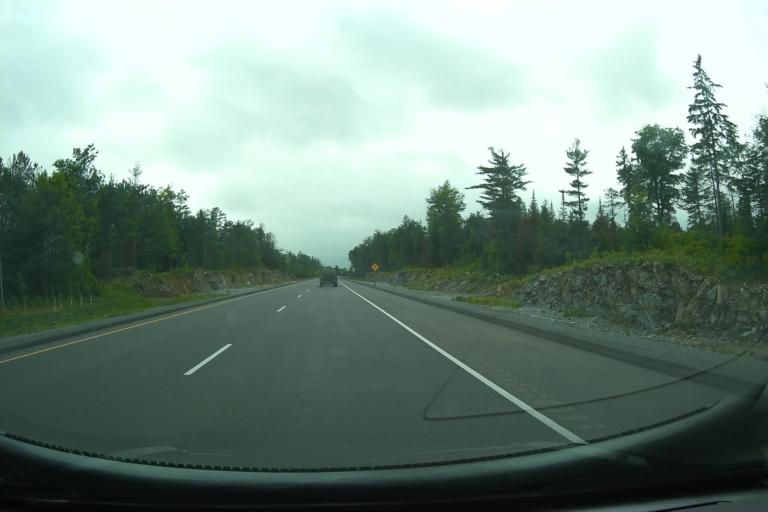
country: CA
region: Ontario
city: Arnprior
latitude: 45.4375
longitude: -76.4454
